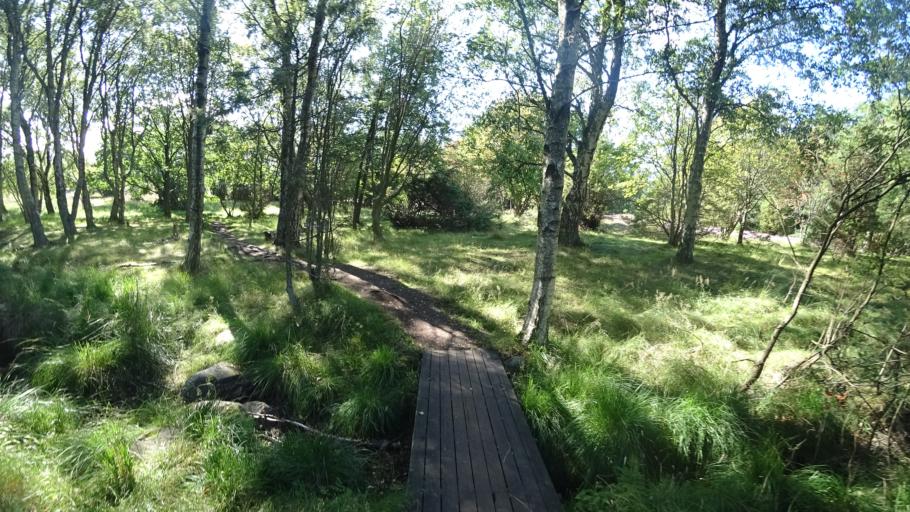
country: SE
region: Vaestra Goetaland
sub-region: Goteborg
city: Styrso
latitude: 57.6045
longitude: 11.7741
